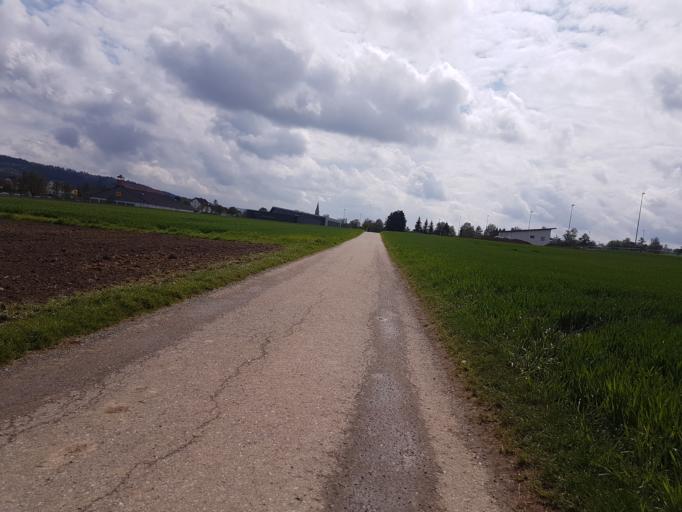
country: DE
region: Baden-Wuerttemberg
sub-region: Freiburg Region
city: Deisslingen
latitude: 48.1205
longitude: 8.6104
